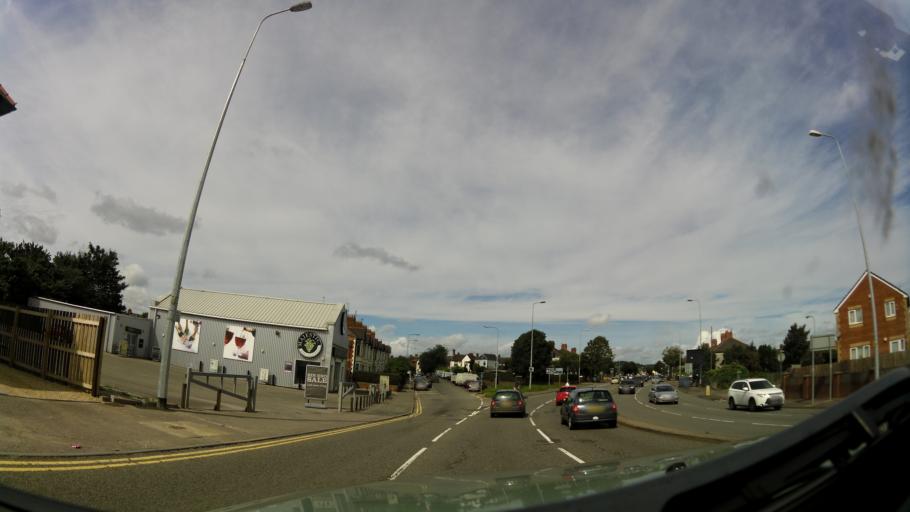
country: GB
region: Wales
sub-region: Cardiff
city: Cardiff
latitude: 51.5087
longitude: -3.2023
